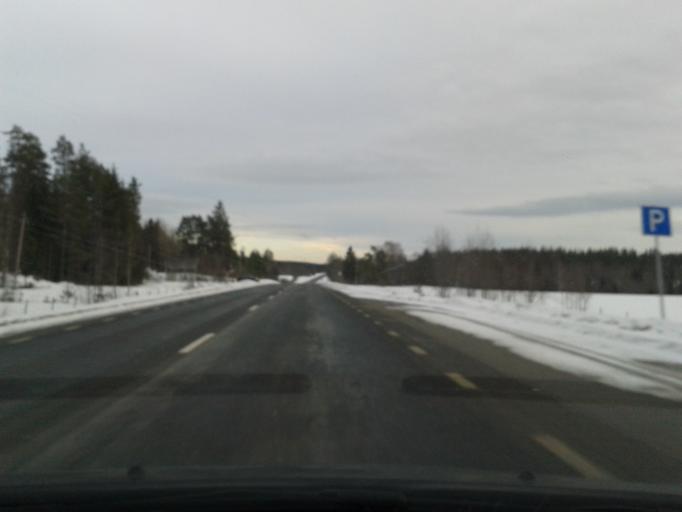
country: SE
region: Vaesternorrland
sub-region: Solleftea Kommun
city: As
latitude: 63.4295
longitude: 16.9467
